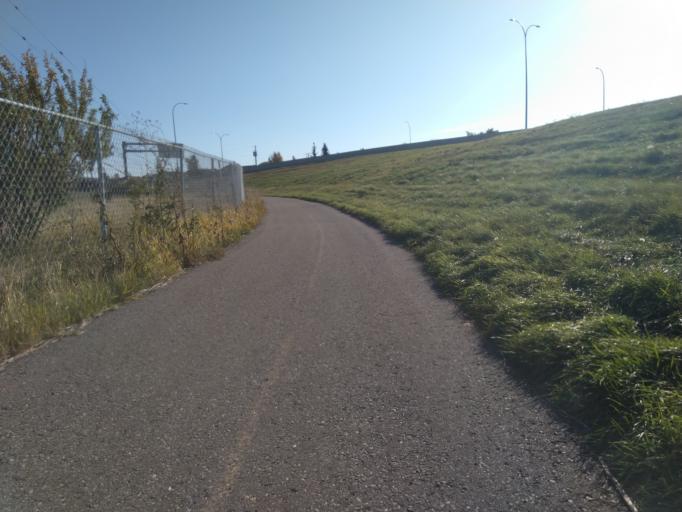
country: CA
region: Alberta
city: Calgary
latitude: 51.1434
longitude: -114.0906
